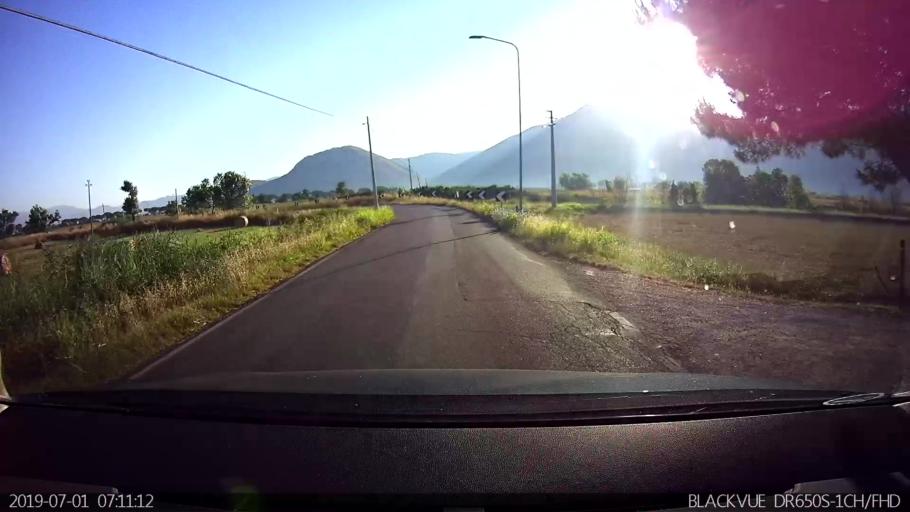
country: IT
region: Latium
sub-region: Provincia di Latina
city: Borgo Hermada
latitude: 41.3181
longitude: 13.1786
